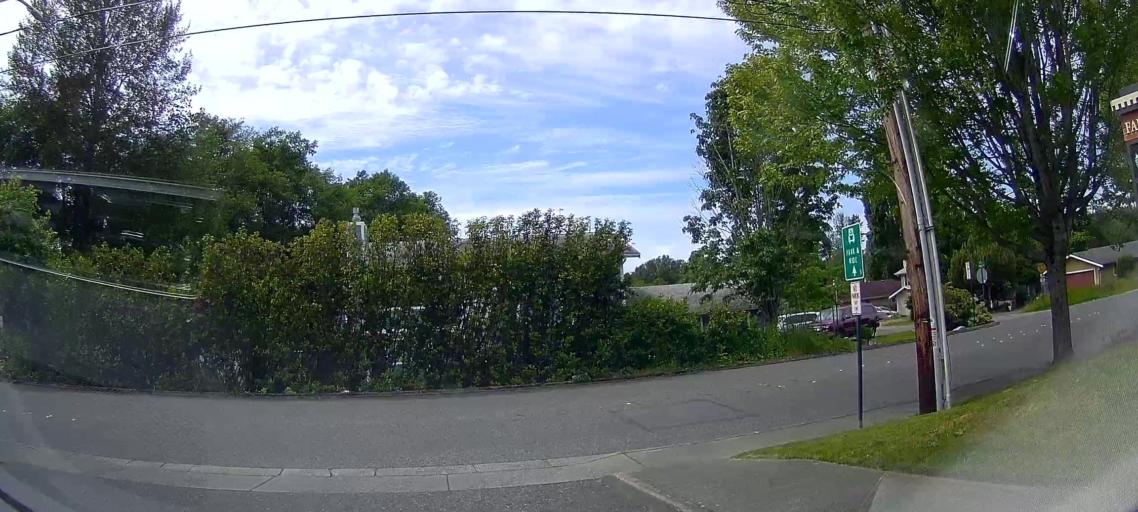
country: US
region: Washington
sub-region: Whatcom County
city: Bellingham
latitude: 48.7152
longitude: -122.4780
